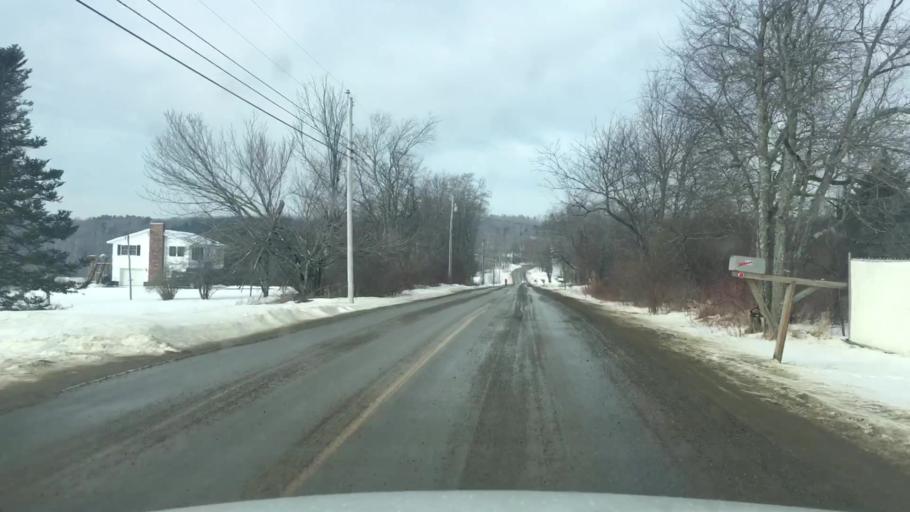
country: US
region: Maine
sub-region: Penobscot County
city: Hermon
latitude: 44.7651
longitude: -68.9545
